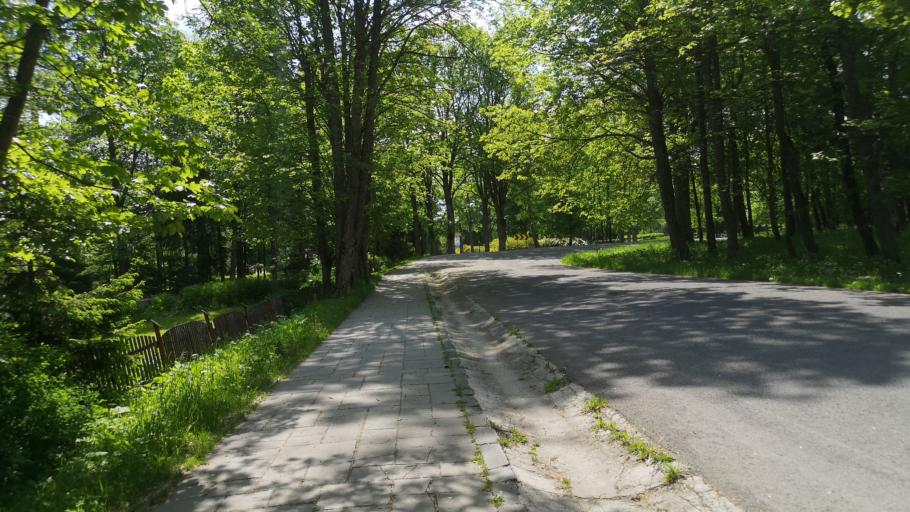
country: SK
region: Presovsky
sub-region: Okres Poprad
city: Vysoke Tatry
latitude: 49.1676
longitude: 20.2775
